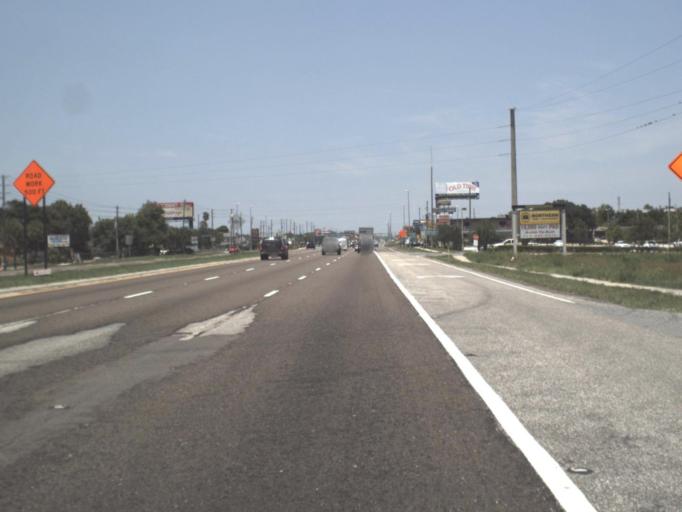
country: US
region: Florida
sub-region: Pasco County
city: Holiday
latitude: 28.1713
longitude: -82.7404
